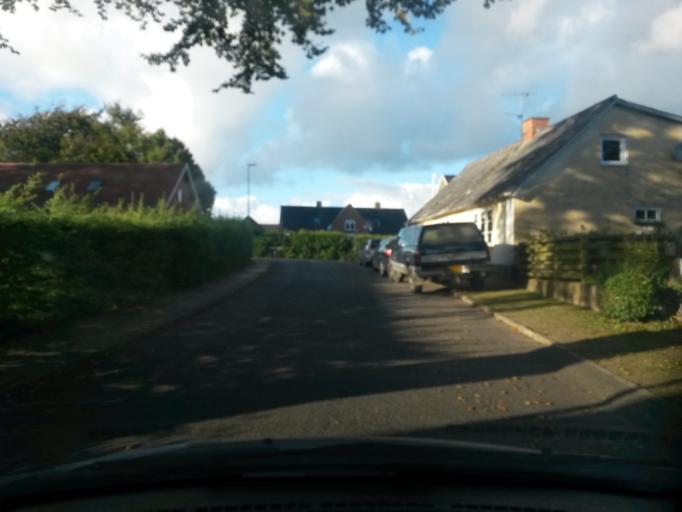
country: DK
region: Central Jutland
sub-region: Silkeborg Kommune
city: Kjellerup
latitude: 56.3369
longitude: 9.4215
